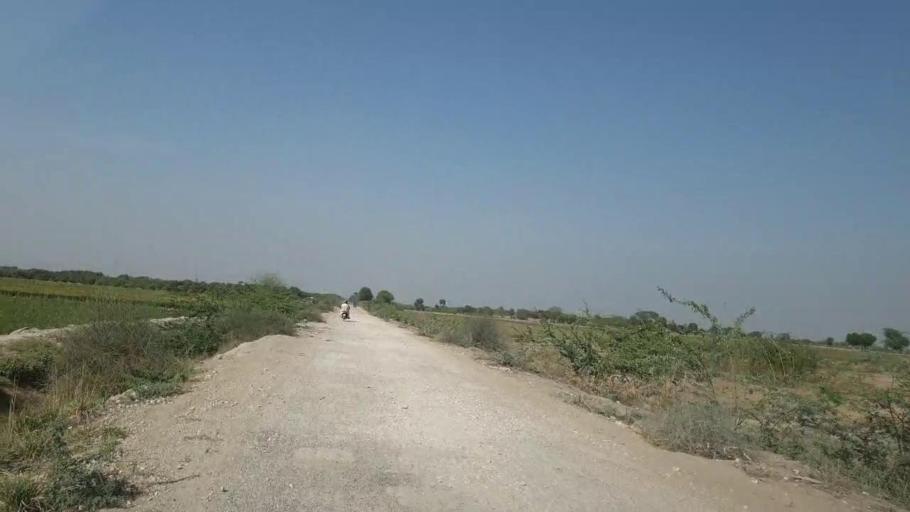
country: PK
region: Sindh
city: Nabisar
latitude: 25.0207
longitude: 69.5243
